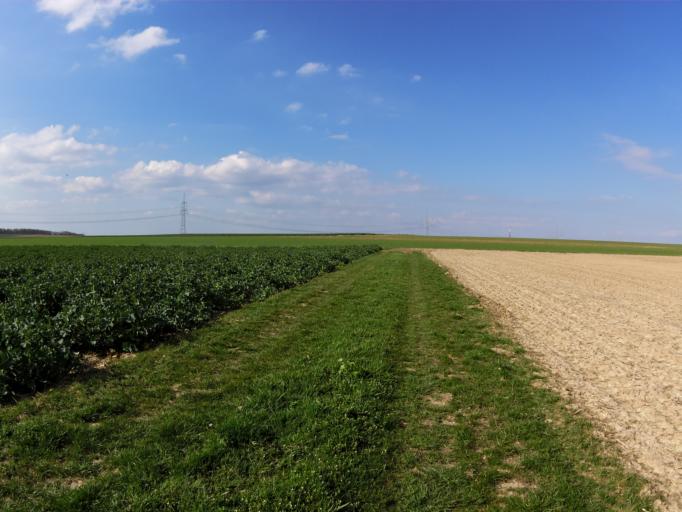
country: DE
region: Bavaria
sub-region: Regierungsbezirk Unterfranken
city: Biebelried
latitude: 49.7968
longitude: 10.0734
